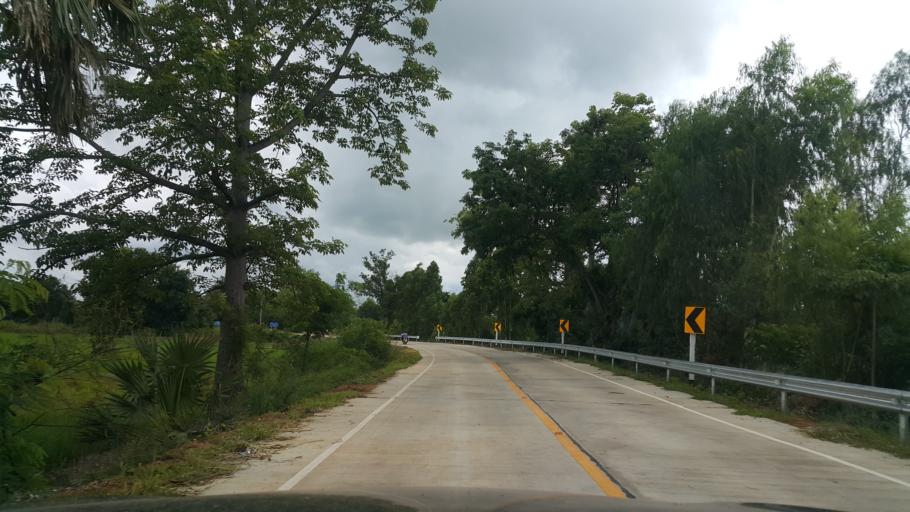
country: TH
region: Sukhothai
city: Kong Krailat
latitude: 16.9268
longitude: 99.8998
